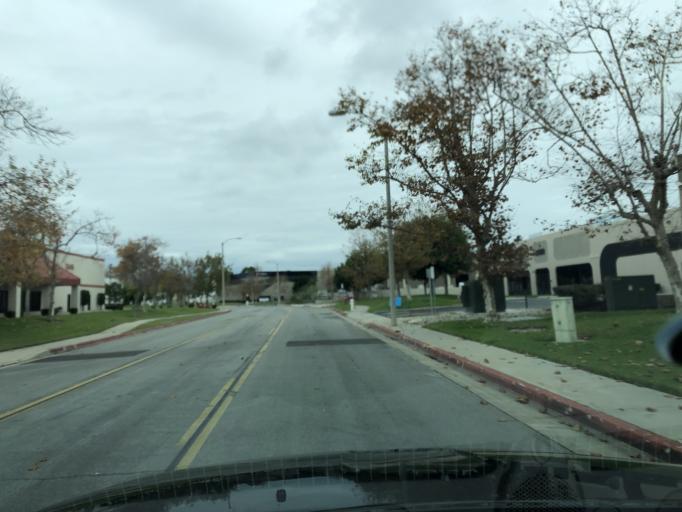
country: US
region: California
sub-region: Orange County
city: Fountain Valley
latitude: 33.6982
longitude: -117.9298
